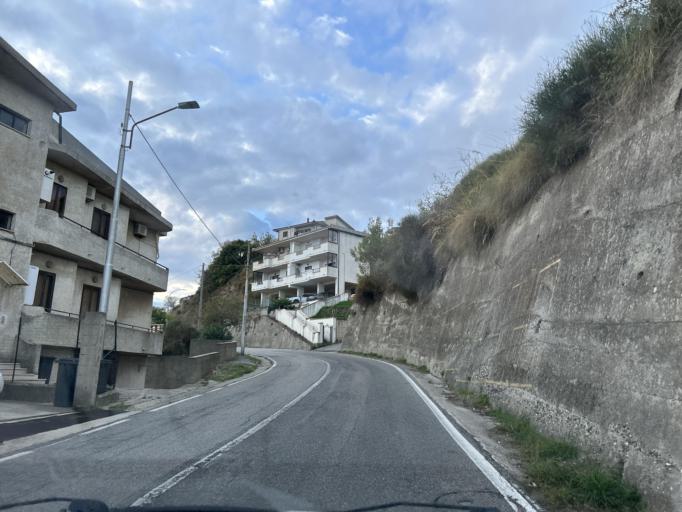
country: IT
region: Calabria
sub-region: Provincia di Catanzaro
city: Montauro
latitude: 38.7500
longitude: 16.5097
